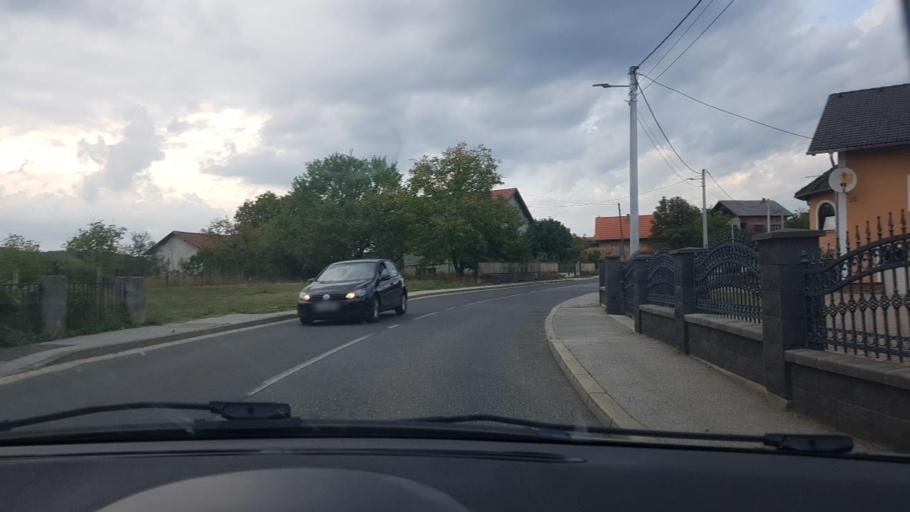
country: HR
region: Grad Zagreb
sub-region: Sesvete
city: Sesvete
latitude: 45.8871
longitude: 16.1736
